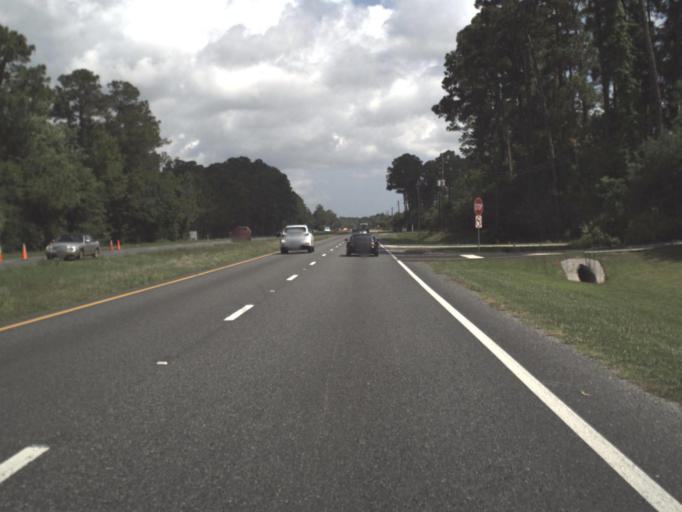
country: US
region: Florida
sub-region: Saint Johns County
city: Saint Augustine Shores
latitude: 29.8015
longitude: -81.3204
